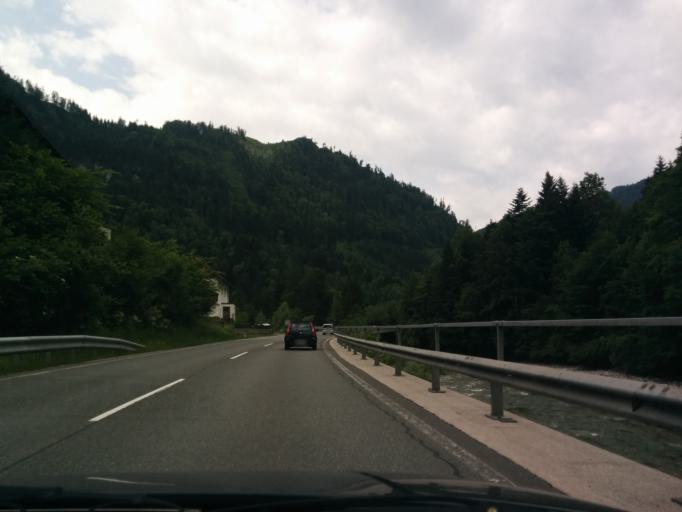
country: AT
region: Salzburg
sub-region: Politischer Bezirk Hallein
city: Abtenau
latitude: 47.5901
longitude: 13.2898
